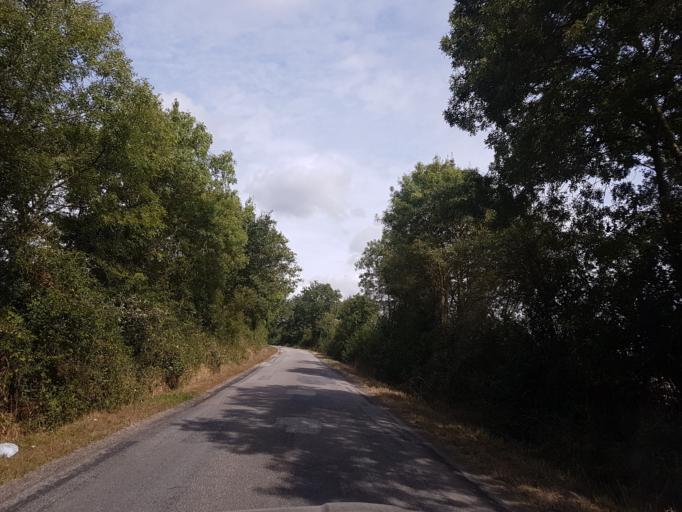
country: FR
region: Pays de la Loire
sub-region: Departement de la Loire-Atlantique
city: Petit-Mars
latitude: 47.3976
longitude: -1.4270
